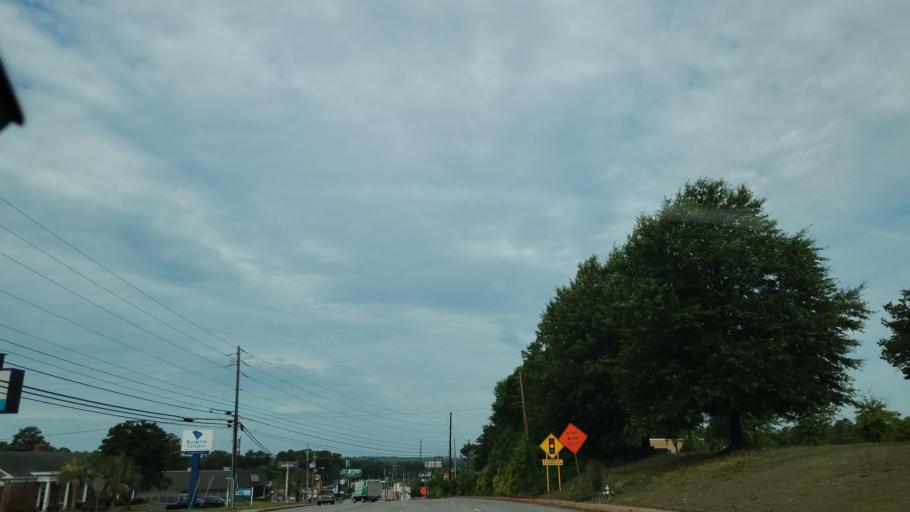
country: US
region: South Carolina
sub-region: Lexington County
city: Saint Andrews
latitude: 34.0308
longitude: -81.0941
